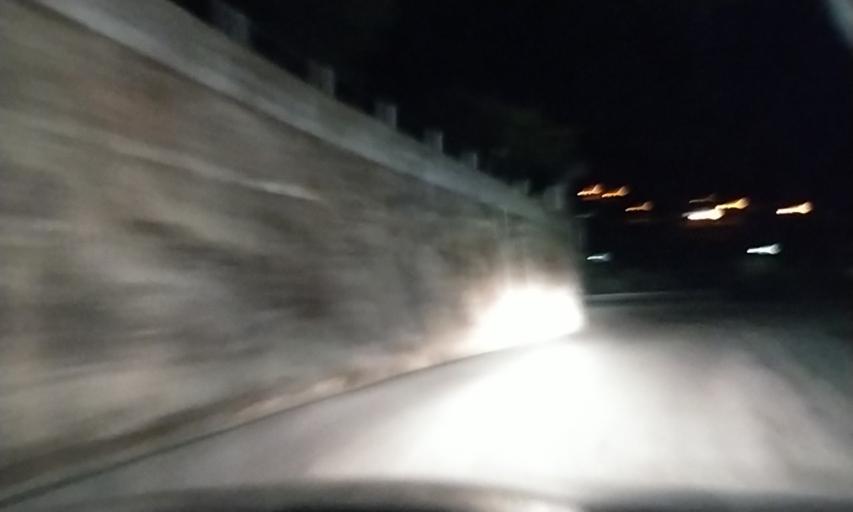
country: PT
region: Vila Real
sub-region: Peso da Regua
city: Godim
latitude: 41.1840
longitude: -7.8148
